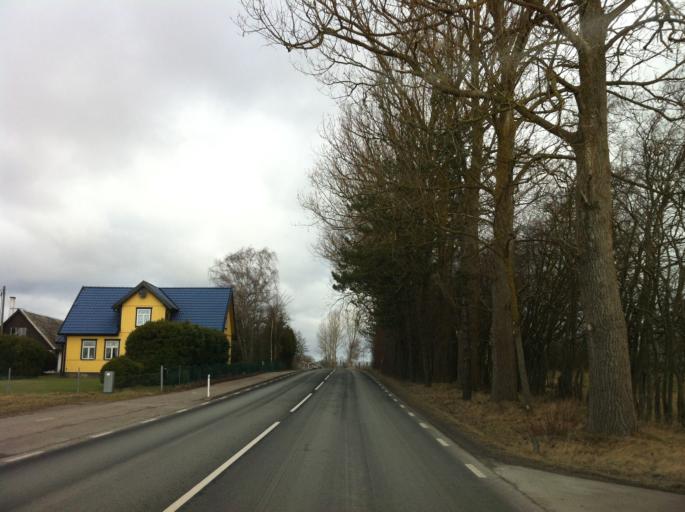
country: SE
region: Skane
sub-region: Angelholms Kommun
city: Strovelstorp
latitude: 56.1736
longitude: 12.8529
